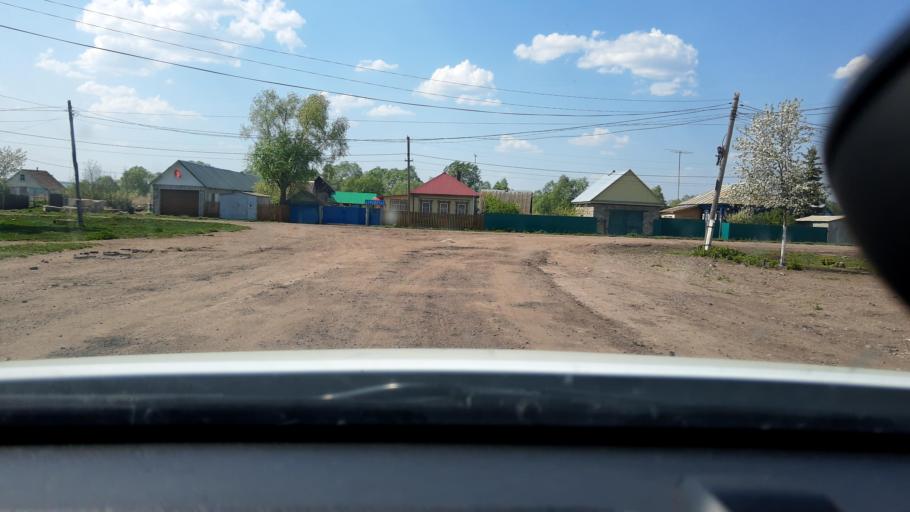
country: RU
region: Bashkortostan
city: Asanovo
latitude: 54.8445
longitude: 55.4515
